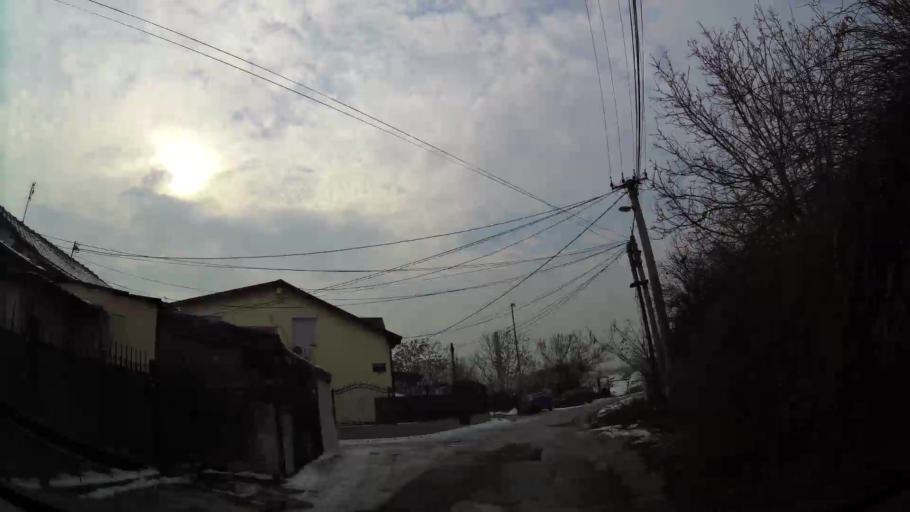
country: MK
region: Cair
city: Cair
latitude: 41.9949
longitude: 21.4608
